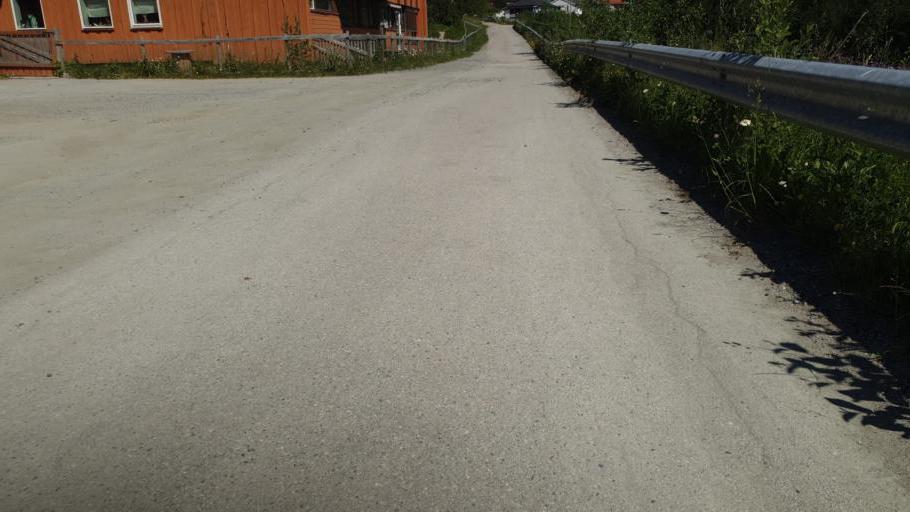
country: NO
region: Sor-Trondelag
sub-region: Trondheim
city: Trondheim
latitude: 63.5554
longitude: 10.2256
